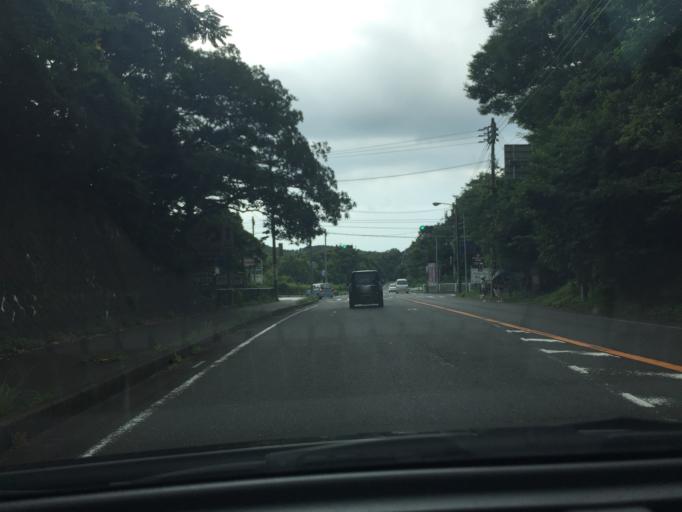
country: JP
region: Shizuoka
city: Ito
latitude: 34.9026
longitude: 139.1205
